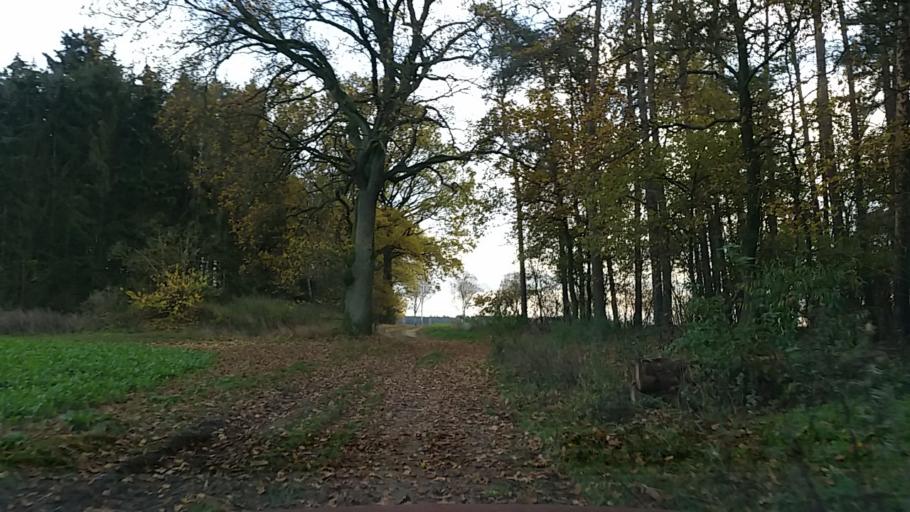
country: DE
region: Lower Saxony
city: Sprakensehl
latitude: 52.7948
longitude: 10.5104
